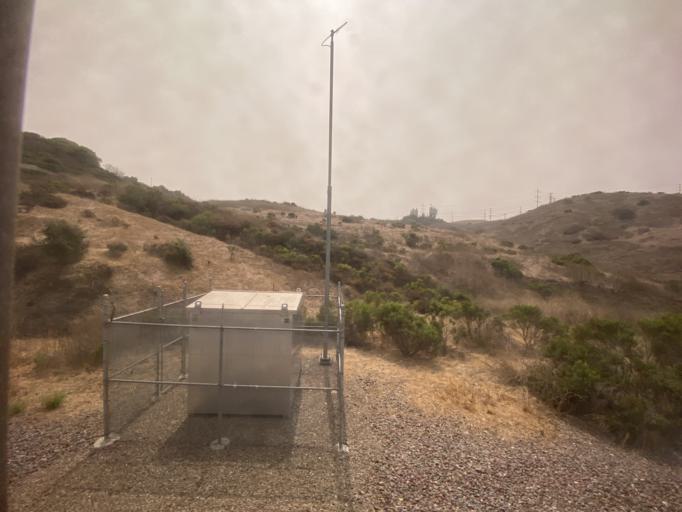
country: US
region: California
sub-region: San Diego County
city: La Jolla
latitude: 32.8883
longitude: -117.1987
